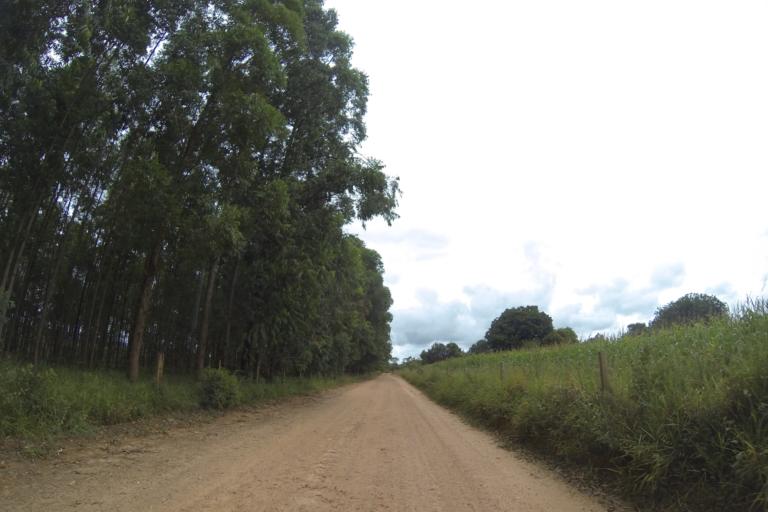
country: BR
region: Minas Gerais
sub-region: Ibia
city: Ibia
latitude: -19.6636
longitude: -46.7001
